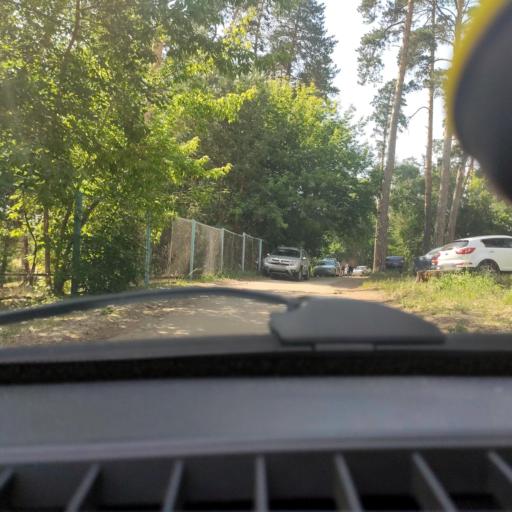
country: RU
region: Samara
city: Tol'yatti
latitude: 53.4734
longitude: 49.3393
